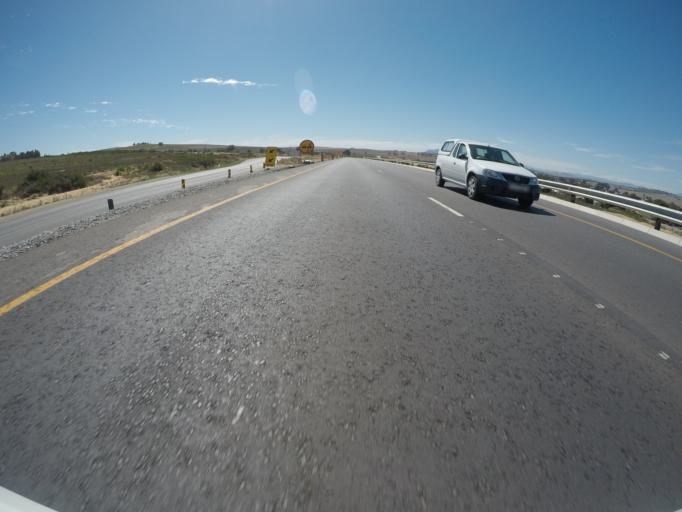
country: ZA
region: Western Cape
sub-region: West Coast District Municipality
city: Malmesbury
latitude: -33.4891
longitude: 18.6713
